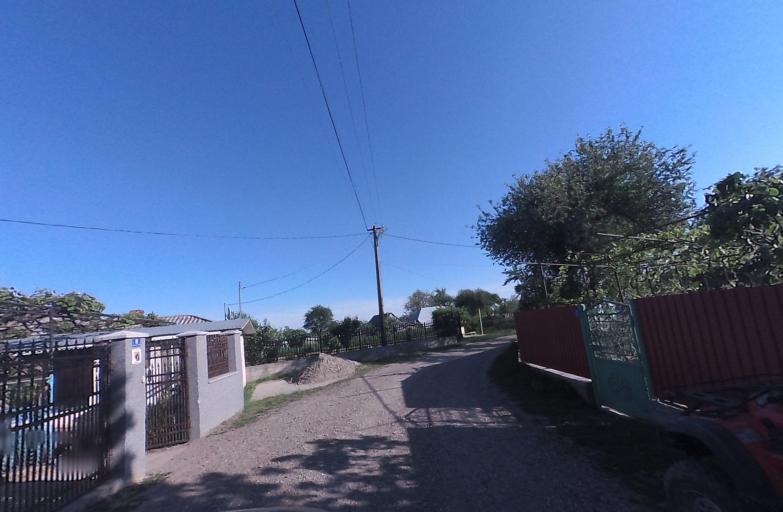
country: RO
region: Neamt
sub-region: Comuna Cordun
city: Pildesti
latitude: 46.9843
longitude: 26.8044
